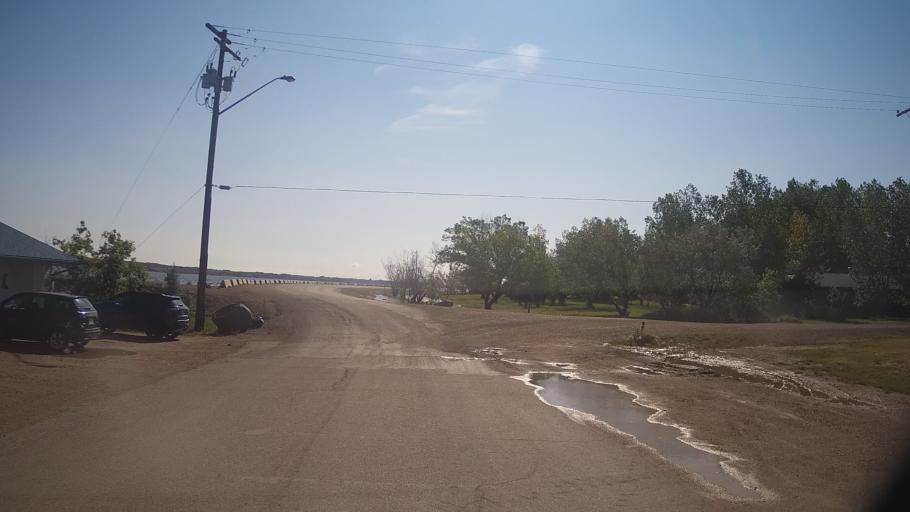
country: CA
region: Saskatchewan
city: Watrous
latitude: 51.7190
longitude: -105.4327
